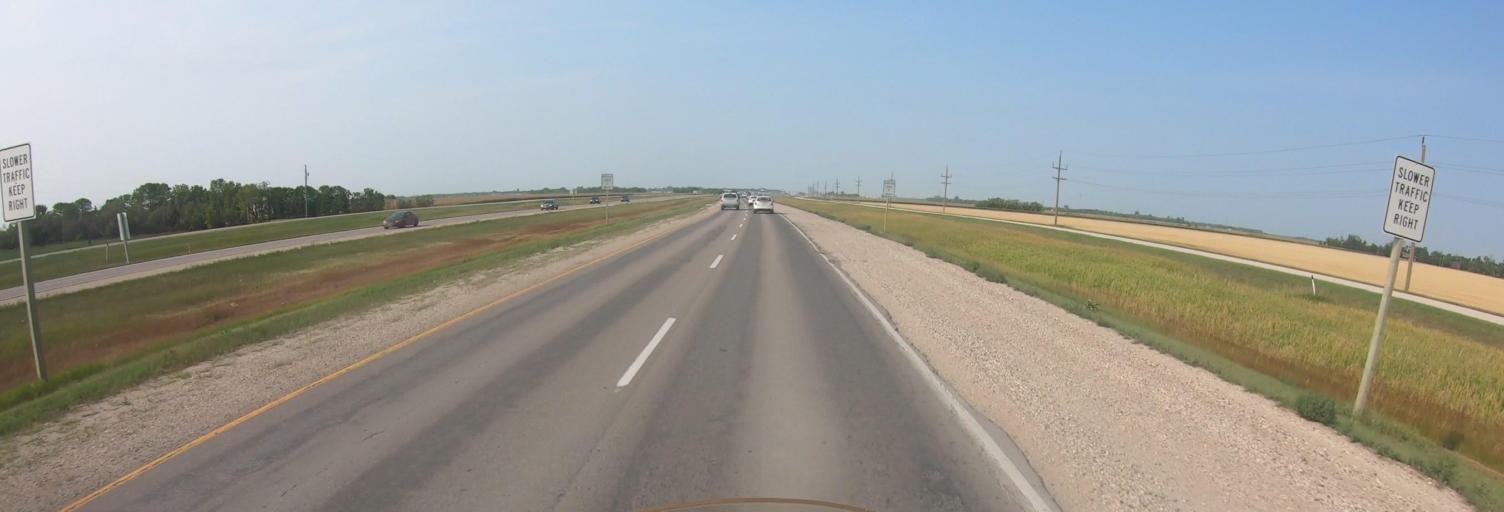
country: CA
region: Manitoba
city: Steinbach
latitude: 49.5774
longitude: -96.6867
